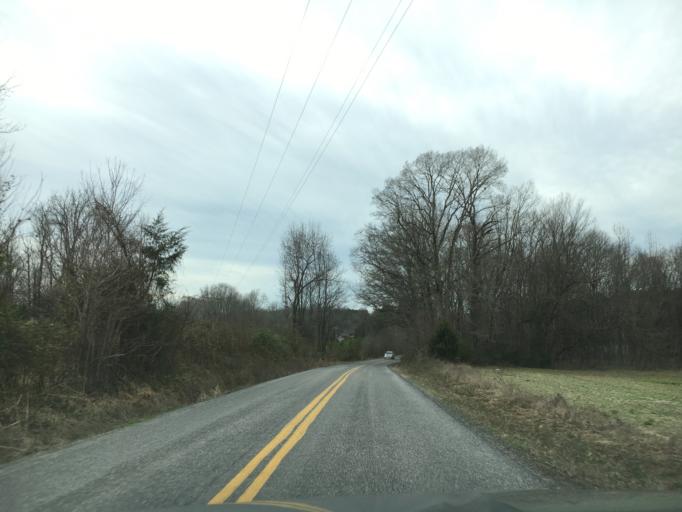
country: US
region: Virginia
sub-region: Amelia County
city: Amelia Court House
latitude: 37.4457
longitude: -77.9941
